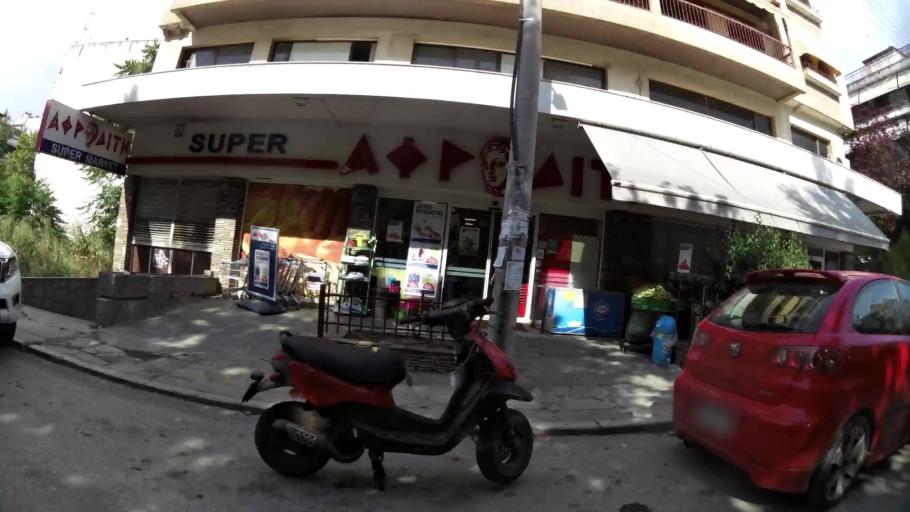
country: GR
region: Central Macedonia
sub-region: Nomos Thessalonikis
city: Kalamaria
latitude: 40.5829
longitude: 22.9567
